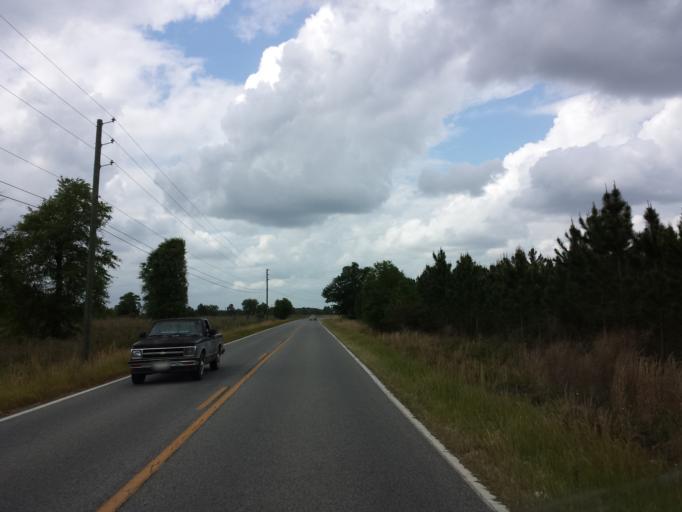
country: US
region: Georgia
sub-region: Cook County
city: Adel
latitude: 31.0861
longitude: -83.4056
